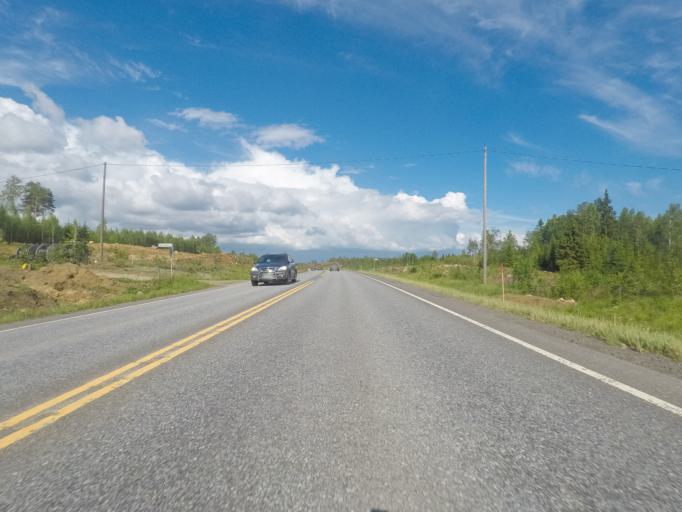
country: FI
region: Southern Savonia
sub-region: Mikkeli
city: Mikkeli
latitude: 61.7572
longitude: 27.5611
